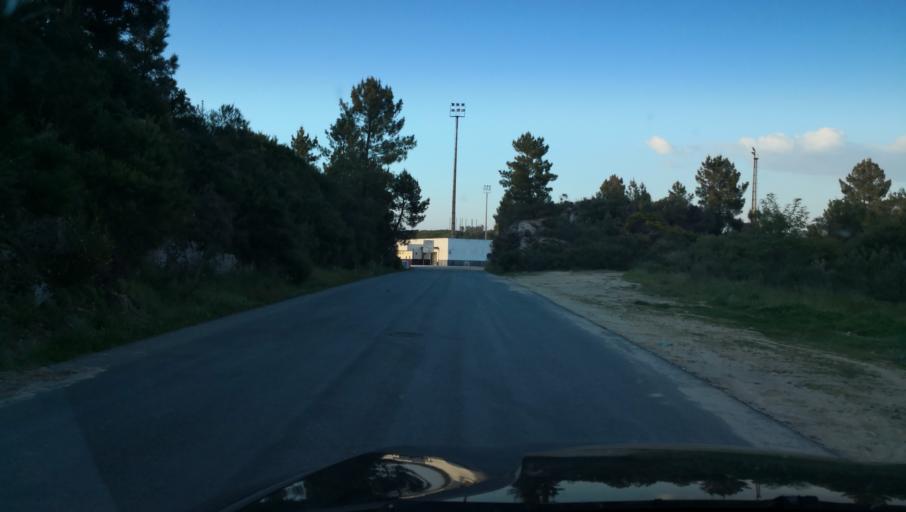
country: PT
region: Vila Real
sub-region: Vila Real
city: Vila Real
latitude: 41.2859
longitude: -7.7570
